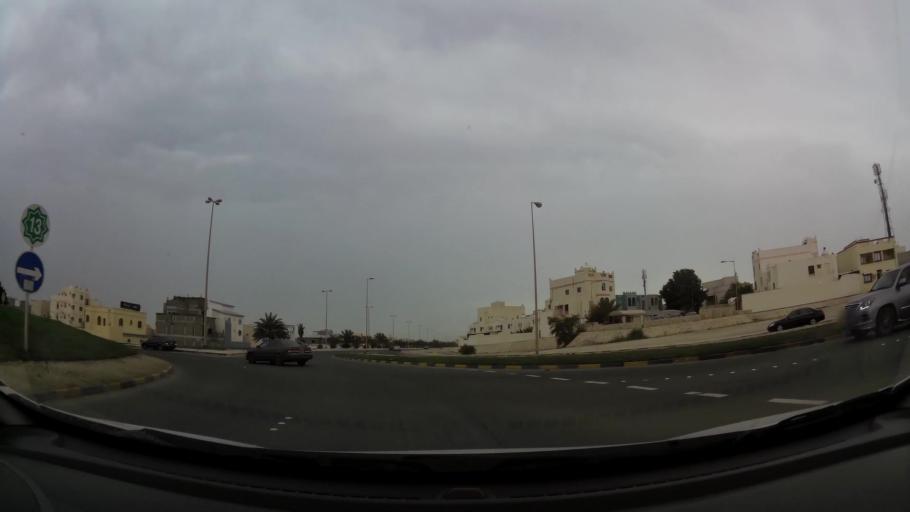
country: BH
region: Central Governorate
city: Madinat Hamad
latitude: 26.0970
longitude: 50.5006
